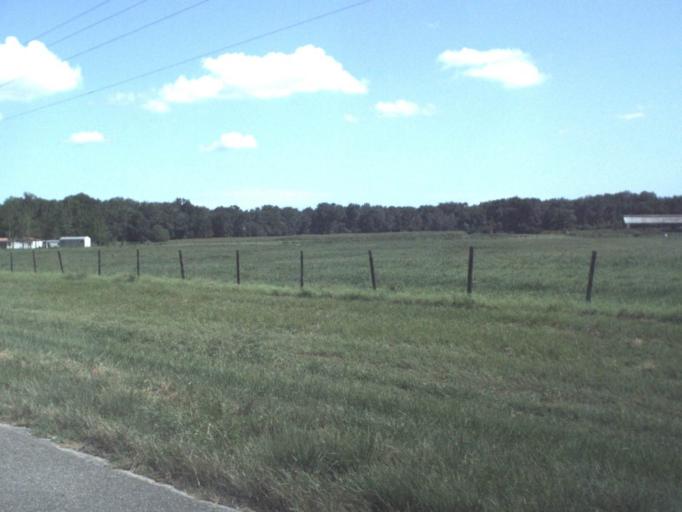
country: US
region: Florida
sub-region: Lafayette County
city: Mayo
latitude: 30.0374
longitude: -83.0688
